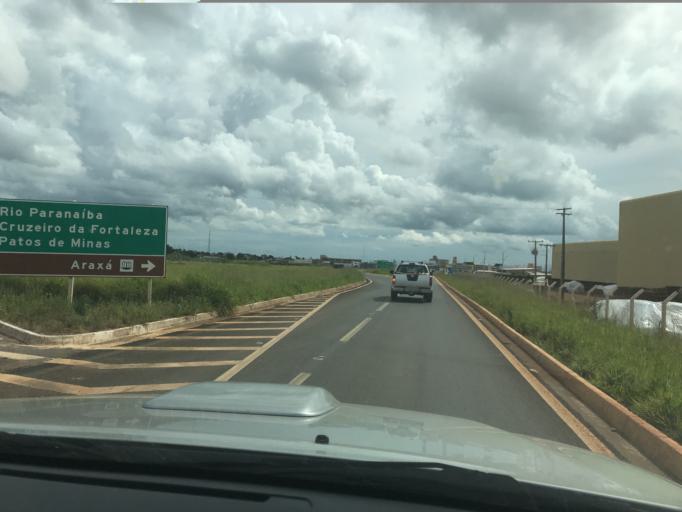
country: BR
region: Minas Gerais
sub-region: Patrocinio
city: Patrocinio
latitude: -19.0971
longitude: -46.6734
